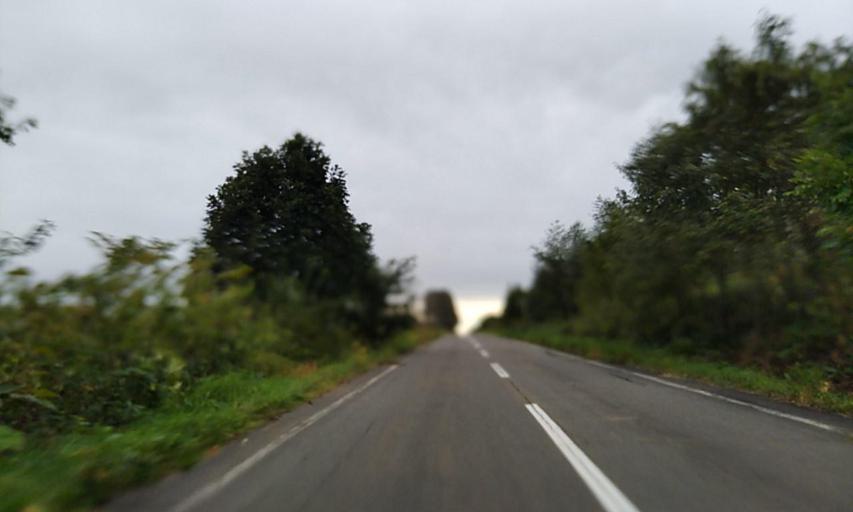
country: JP
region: Hokkaido
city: Obihiro
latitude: 42.6676
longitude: 143.0619
